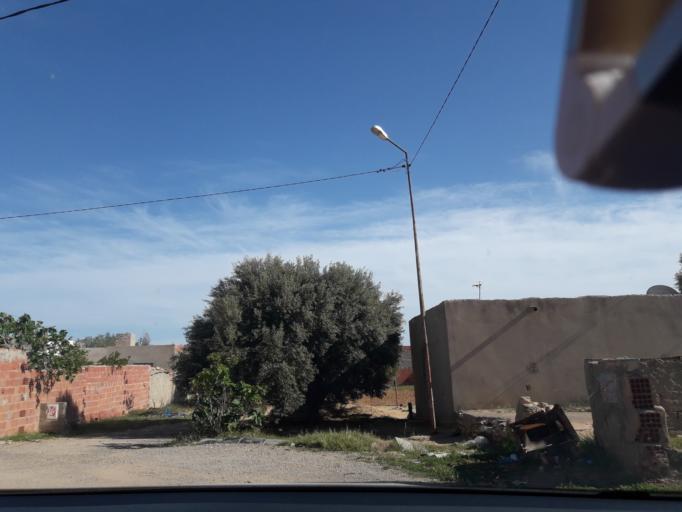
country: TN
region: Safaqis
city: Sfax
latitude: 34.7385
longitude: 10.5191
